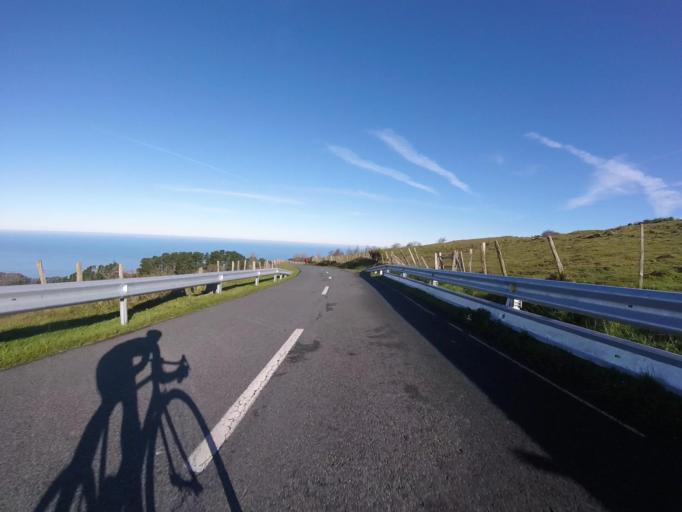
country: ES
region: Basque Country
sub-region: Provincia de Guipuzcoa
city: Fuenterrabia
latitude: 43.3559
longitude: -1.8409
